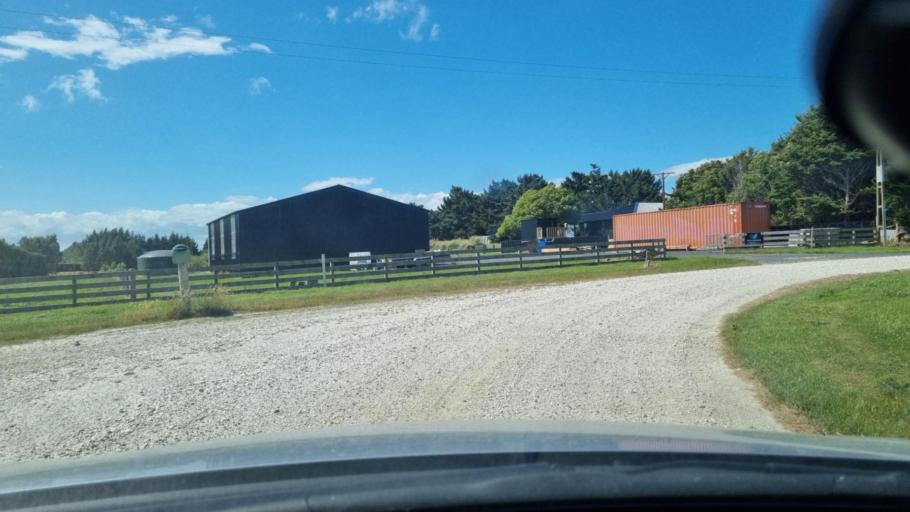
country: NZ
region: Southland
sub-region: Invercargill City
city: Invercargill
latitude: -46.4325
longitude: 168.4100
